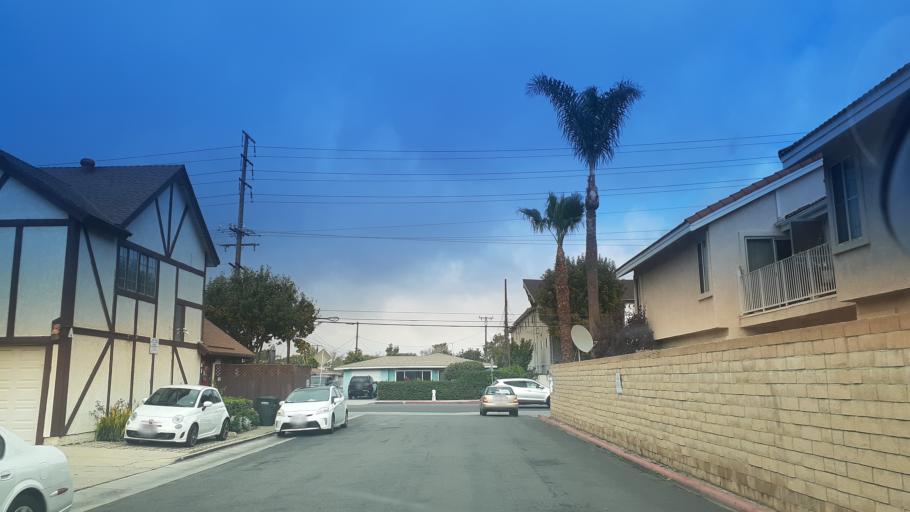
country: US
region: California
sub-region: Orange County
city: Costa Mesa
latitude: 33.6557
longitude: -117.9209
